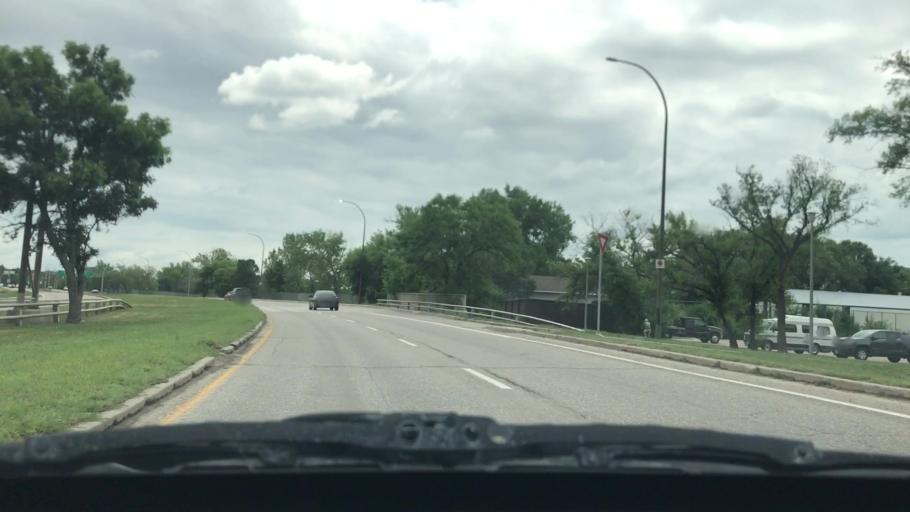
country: CA
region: Manitoba
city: Winnipeg
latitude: 49.8528
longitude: -97.1249
